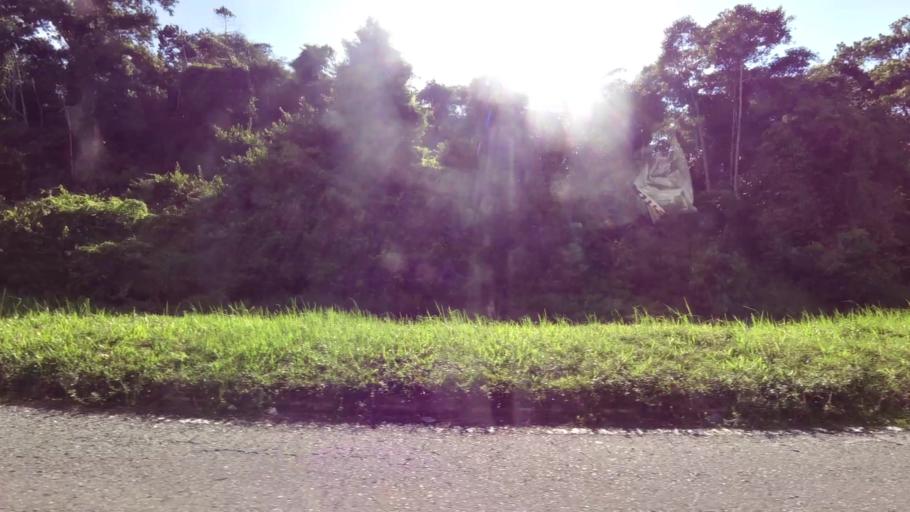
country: BN
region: Brunei and Muara
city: Bandar Seri Begawan
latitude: 4.9772
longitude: 114.9639
